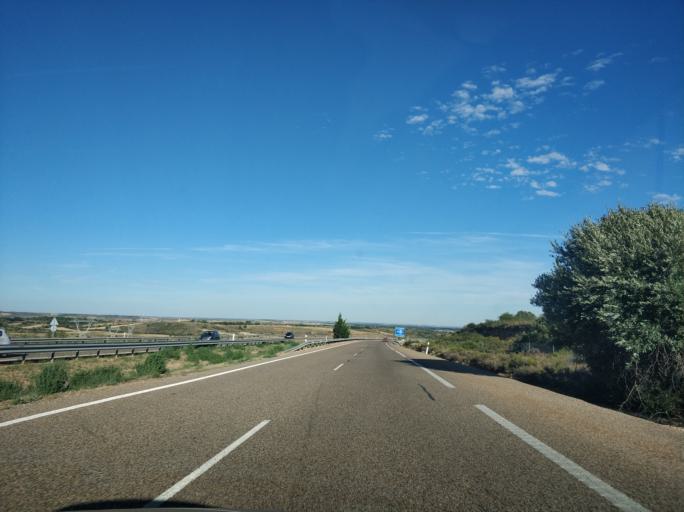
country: ES
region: Castille and Leon
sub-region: Provincia de Leon
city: Valverde de la Virgen
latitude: 42.5567
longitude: -5.6330
